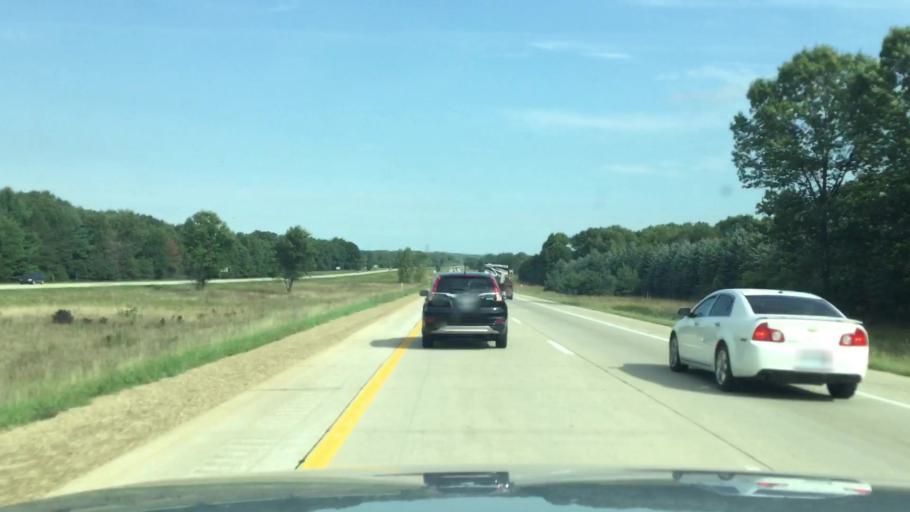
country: US
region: Michigan
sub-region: Allegan County
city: Plainwell
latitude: 42.3878
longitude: -85.6568
